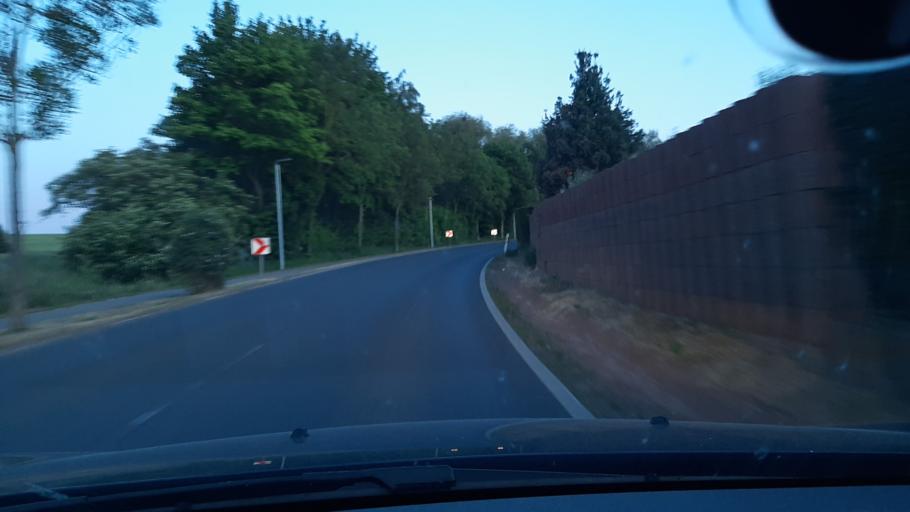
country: DE
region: North Rhine-Westphalia
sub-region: Regierungsbezirk Koln
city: Mechernich
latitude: 50.6151
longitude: 6.6587
